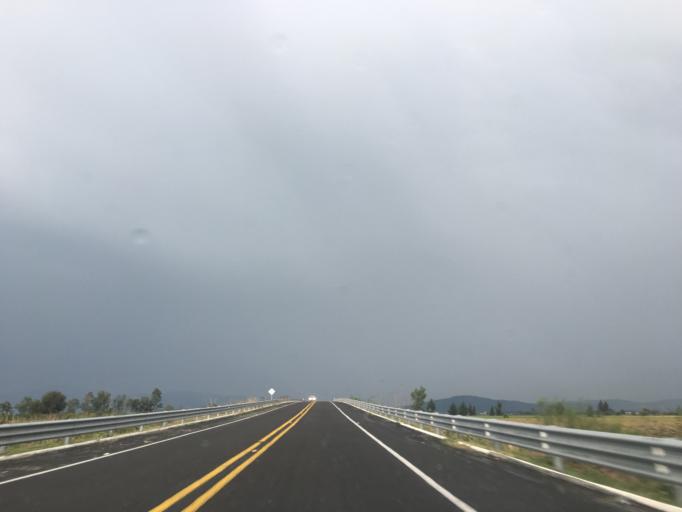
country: MX
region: Michoacan
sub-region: Alvaro Obregon
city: Lazaro Cardenas (La Purisima)
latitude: 19.8741
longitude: -101.0075
